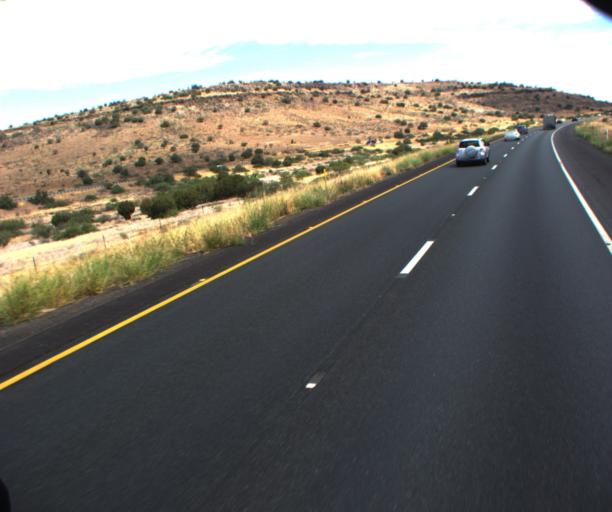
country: US
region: Arizona
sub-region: Yavapai County
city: Camp Verde
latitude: 34.4789
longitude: -112.0196
